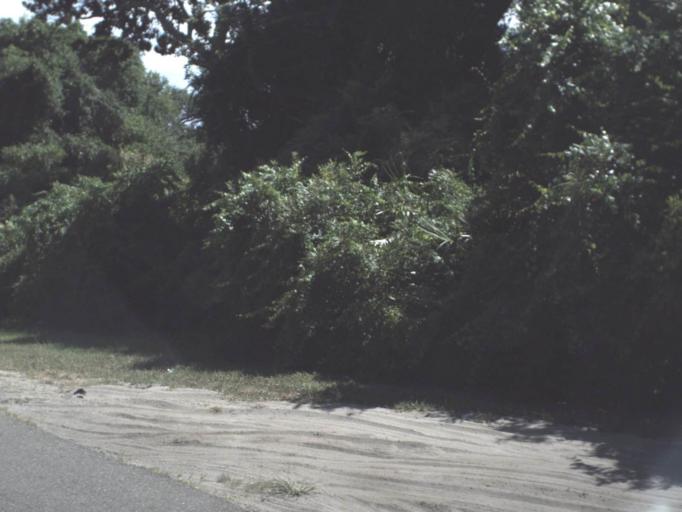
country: US
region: Florida
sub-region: Nassau County
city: Fernandina Beach
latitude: 30.5460
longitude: -81.4455
